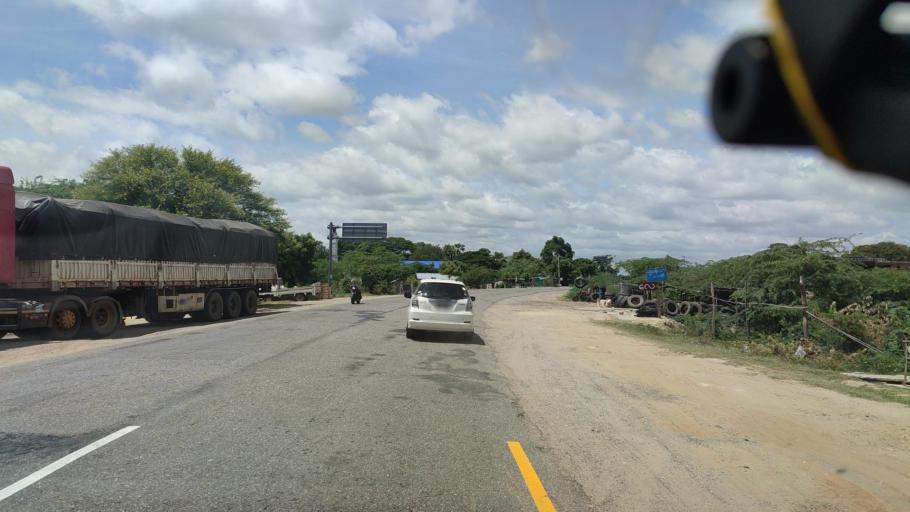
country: MM
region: Mandalay
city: Meiktila
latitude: 20.8568
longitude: 95.9573
